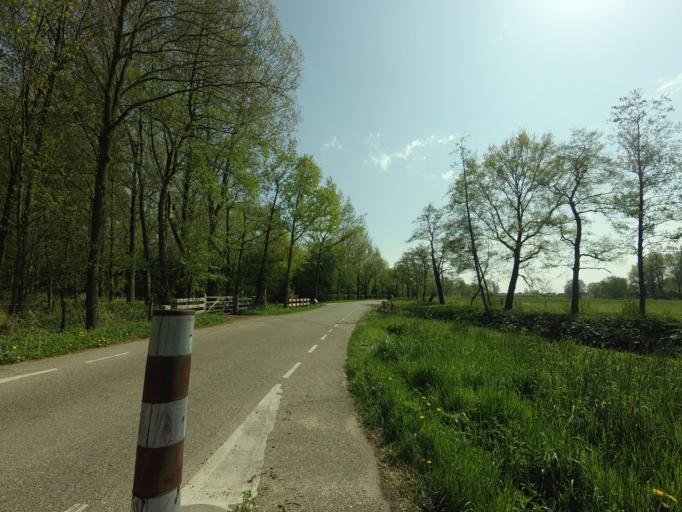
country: NL
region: Utrecht
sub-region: Gemeente Utrechtse Heuvelrug
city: Driebergen-Rijsenburg
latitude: 52.0539
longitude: 5.2456
